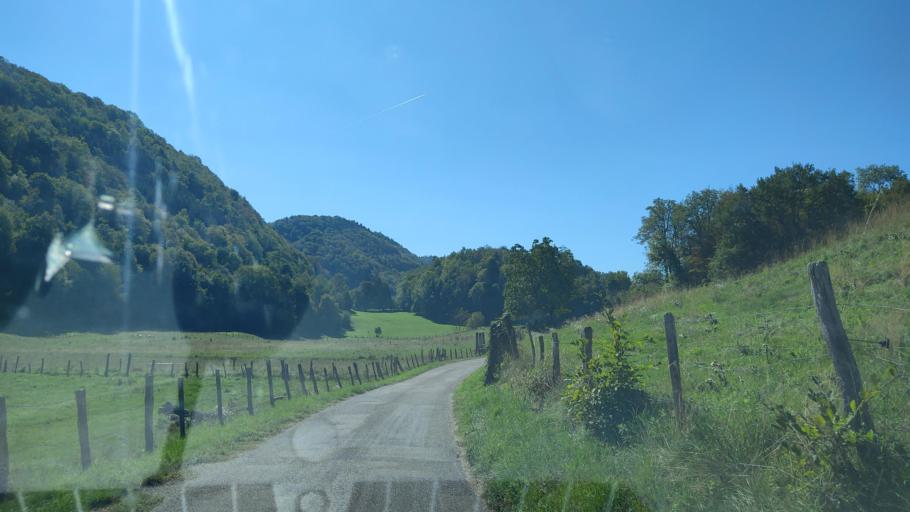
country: FR
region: Rhone-Alpes
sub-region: Departement de la Savoie
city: La Bridoire
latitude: 45.5335
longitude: 5.7539
